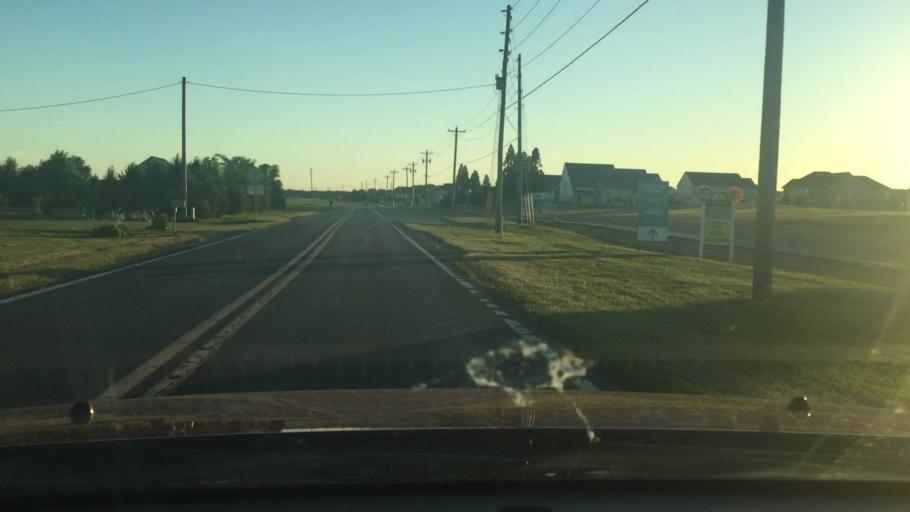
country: US
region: Delaware
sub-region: Kent County
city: Woodside East
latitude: 39.0519
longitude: -75.5197
